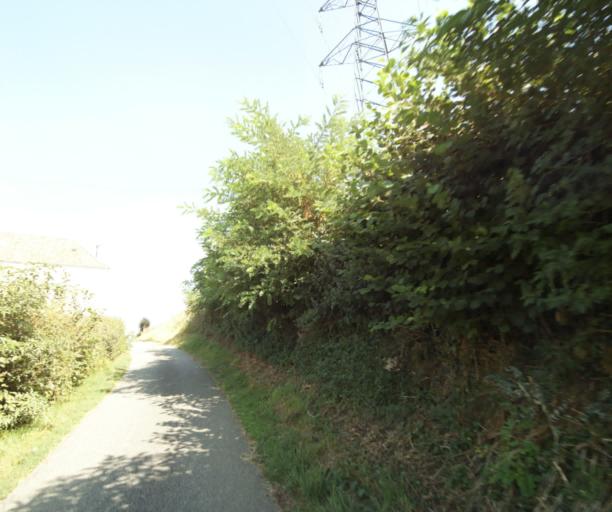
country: FR
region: Bourgogne
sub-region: Departement de Saone-et-Loire
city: Tournus
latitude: 46.5604
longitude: 4.8899
